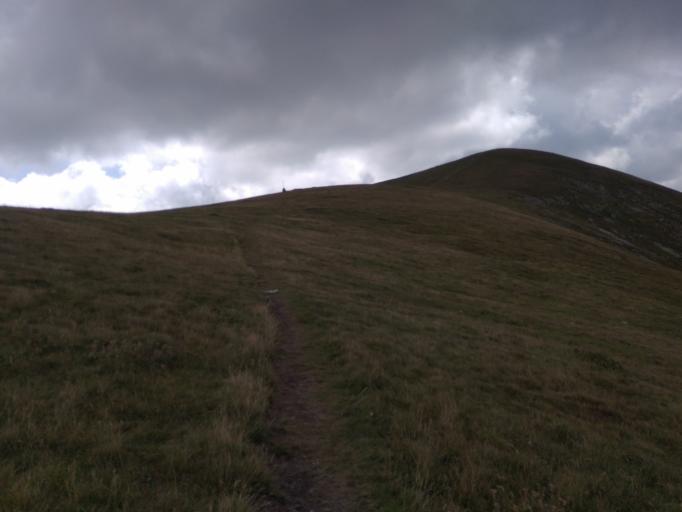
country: BG
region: Plovdiv
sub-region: Obshtina Karlovo
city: Karlovo
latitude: 42.7224
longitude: 24.7852
